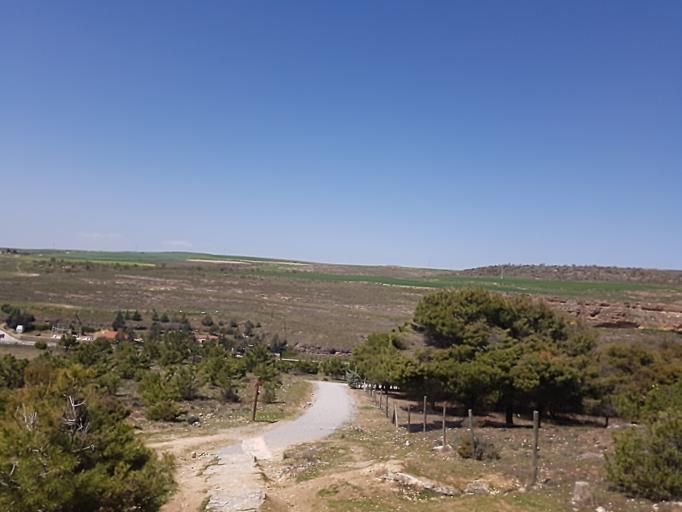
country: ES
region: Castille and Leon
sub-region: Provincia de Segovia
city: Segovia
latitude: 40.9532
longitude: -4.1356
